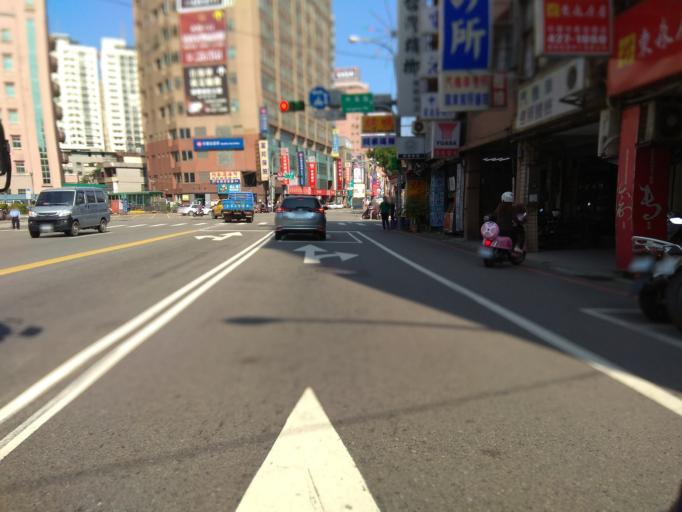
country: TW
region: Taiwan
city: Taoyuan City
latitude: 24.9589
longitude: 121.2244
